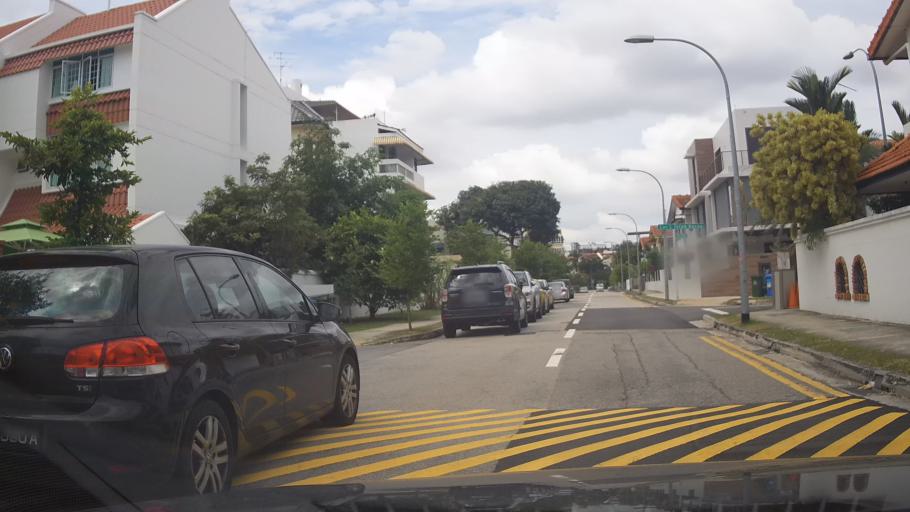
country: SG
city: Singapore
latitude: 1.3116
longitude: 103.9100
